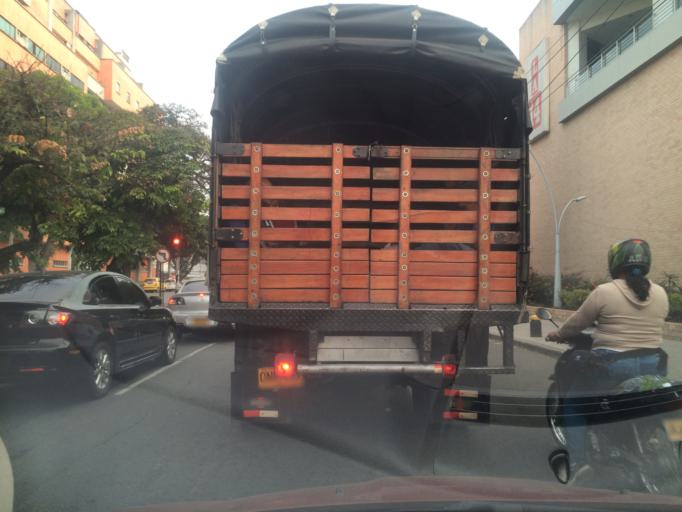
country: CO
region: Valle del Cauca
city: Cali
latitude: 3.4267
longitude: -76.5378
